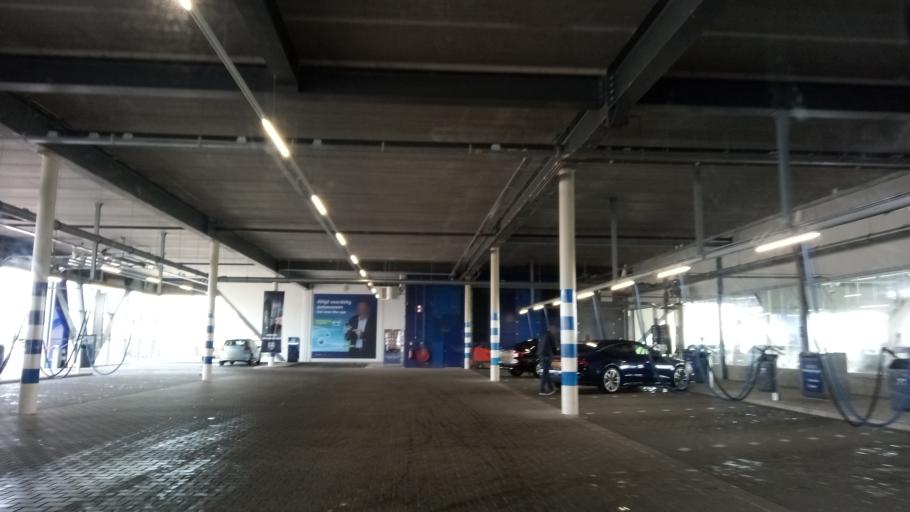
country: NL
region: North Holland
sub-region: Gemeente Heerhugowaard
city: Heerhugowaard
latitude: 52.6816
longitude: 4.8284
